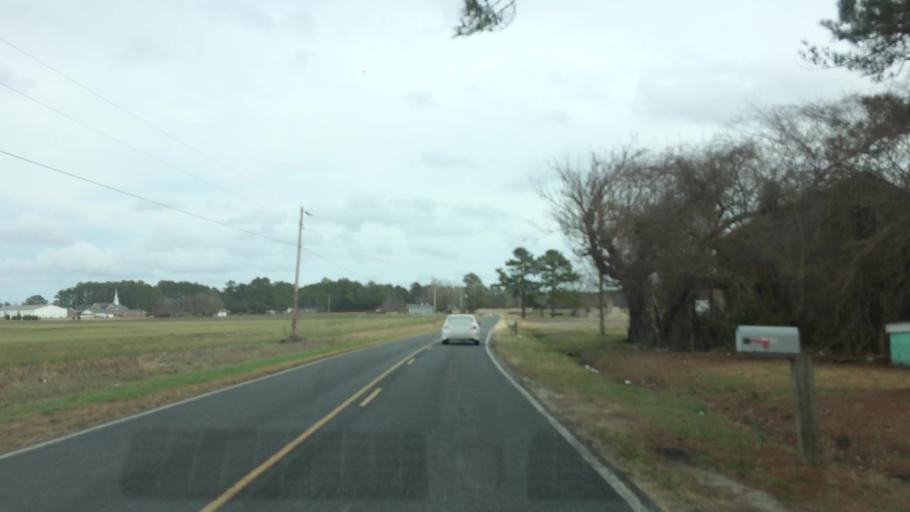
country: US
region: North Carolina
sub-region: Pitt County
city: Winterville
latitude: 35.4901
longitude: -77.3596
